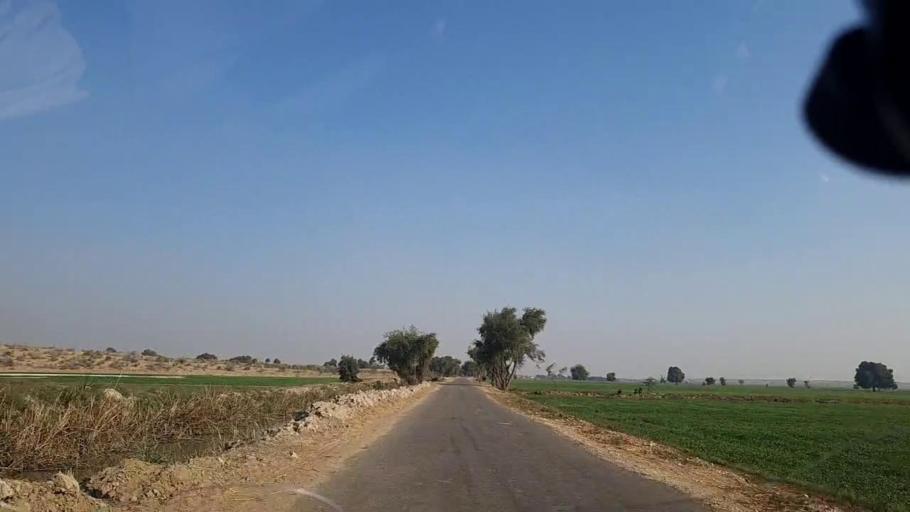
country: PK
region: Sindh
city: Khanpur
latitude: 27.6813
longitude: 69.5543
